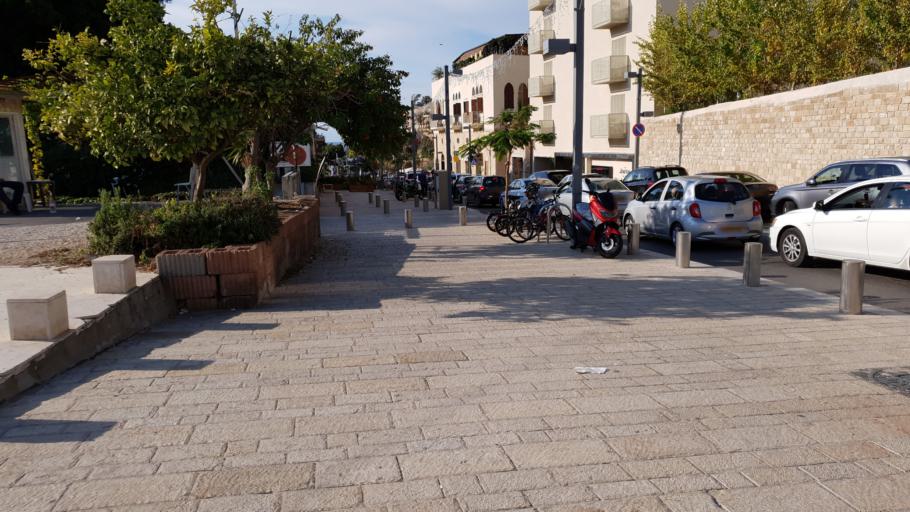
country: IL
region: Tel Aviv
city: Yafo
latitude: 32.0522
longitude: 34.7529
